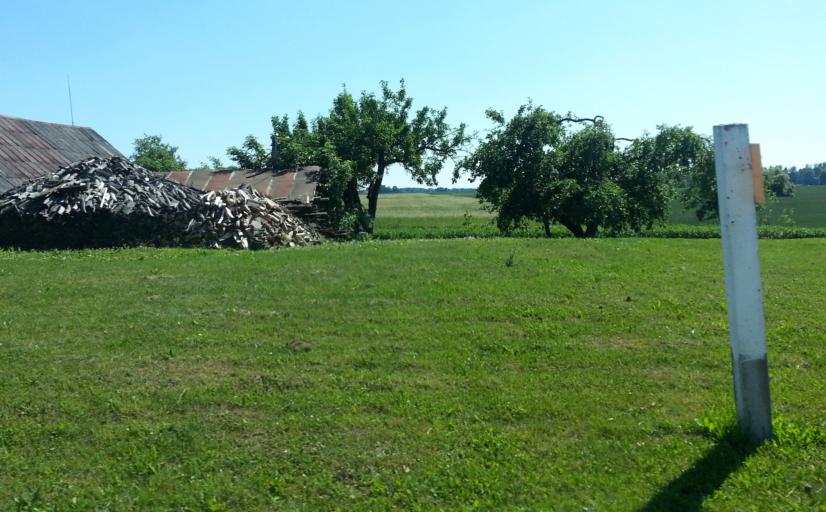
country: LT
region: Panevezys
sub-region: Birzai
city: Birzai
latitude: 56.2131
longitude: 24.6715
